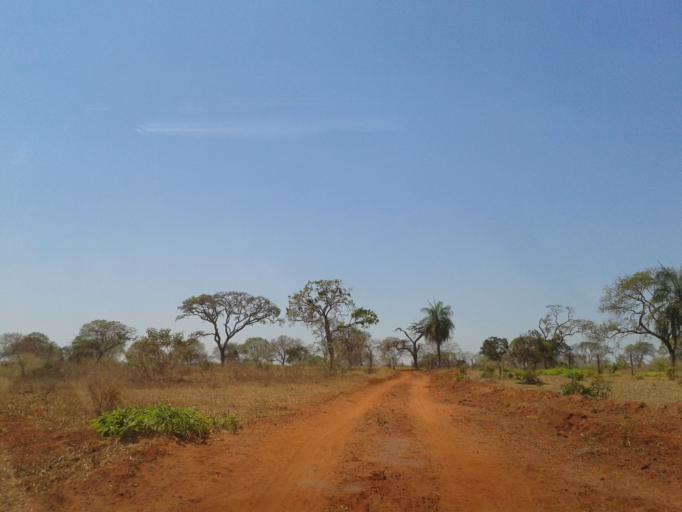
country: BR
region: Minas Gerais
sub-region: Ituiutaba
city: Ituiutaba
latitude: -19.0684
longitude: -49.3680
